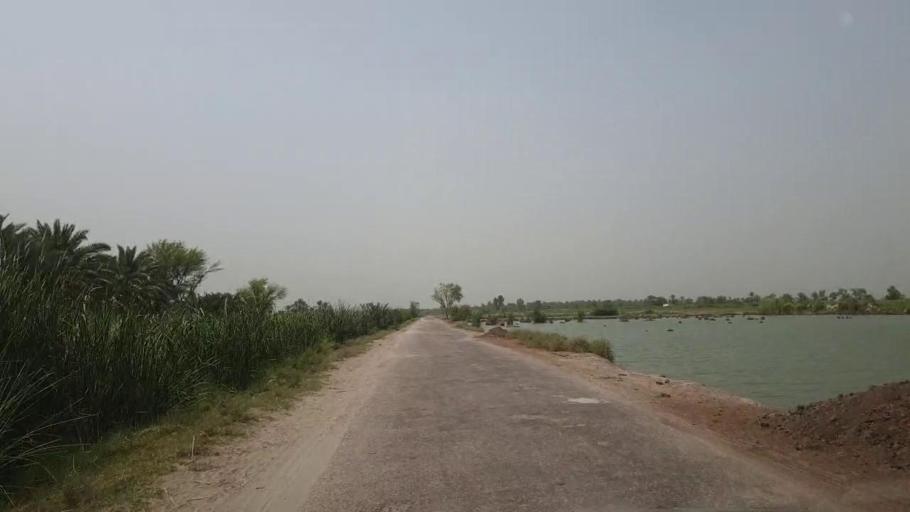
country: PK
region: Sindh
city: Gambat
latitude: 27.3913
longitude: 68.5503
